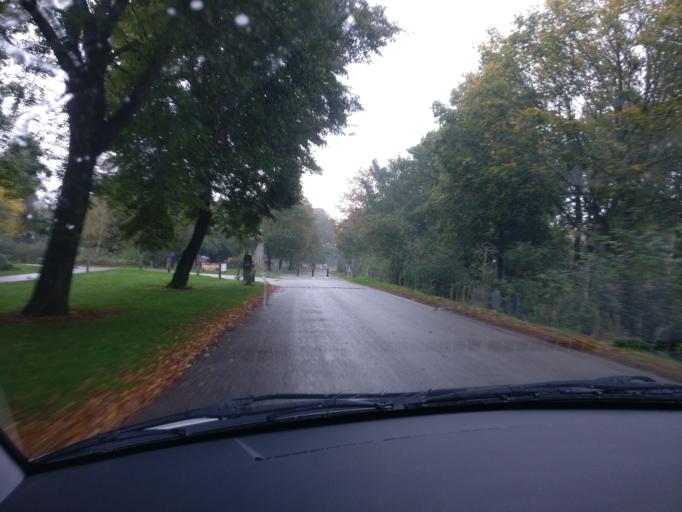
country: GB
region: England
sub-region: Peterborough
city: Castor
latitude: 52.5613
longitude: -0.3058
